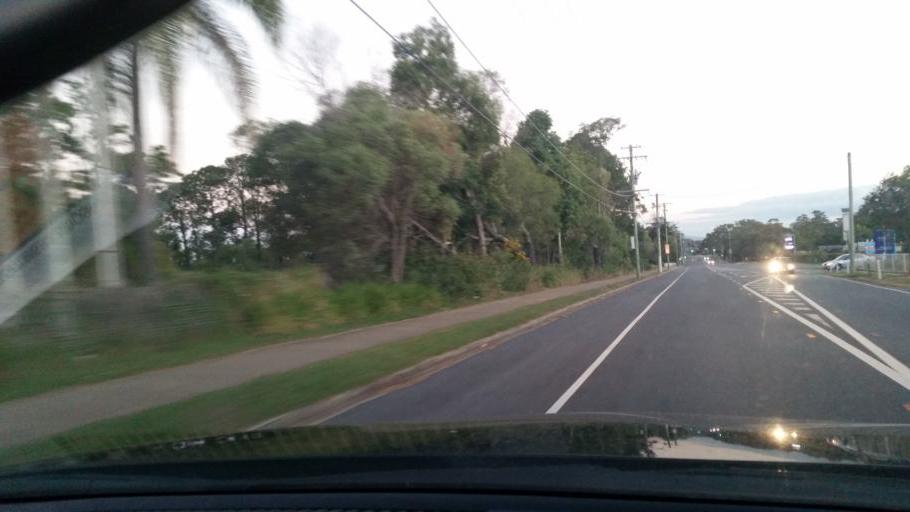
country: AU
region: Queensland
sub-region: Logan
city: Rochedale South
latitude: -27.5819
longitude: 153.1249
